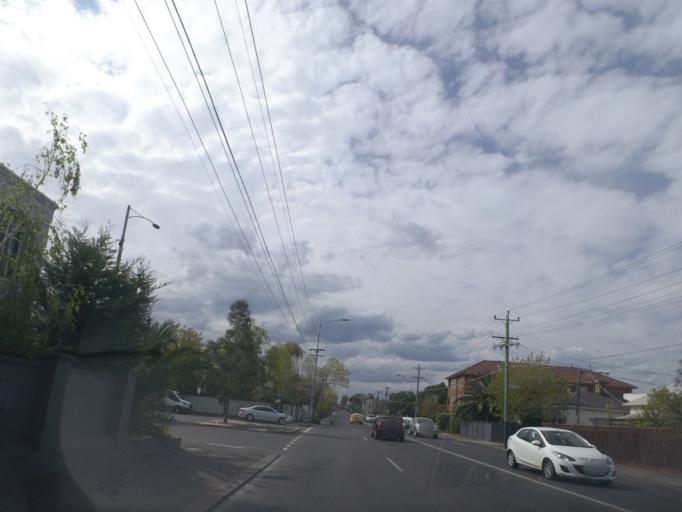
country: AU
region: Victoria
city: Windsor
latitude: -37.8434
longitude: 144.9854
